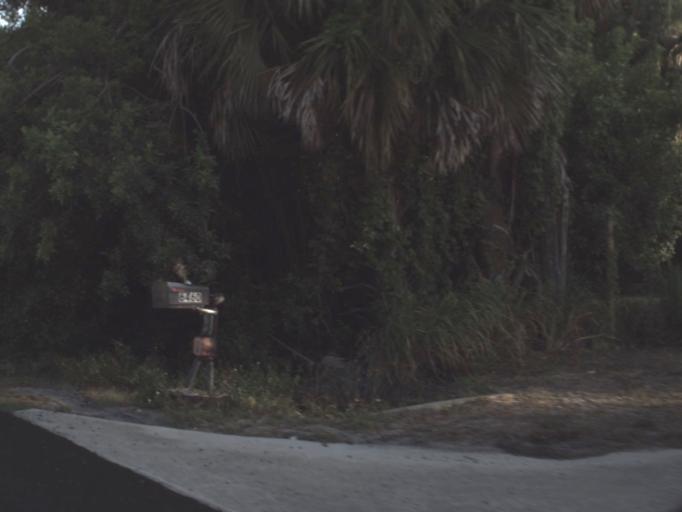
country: US
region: Florida
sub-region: Brevard County
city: South Patrick Shores
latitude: 28.2166
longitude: -80.6676
